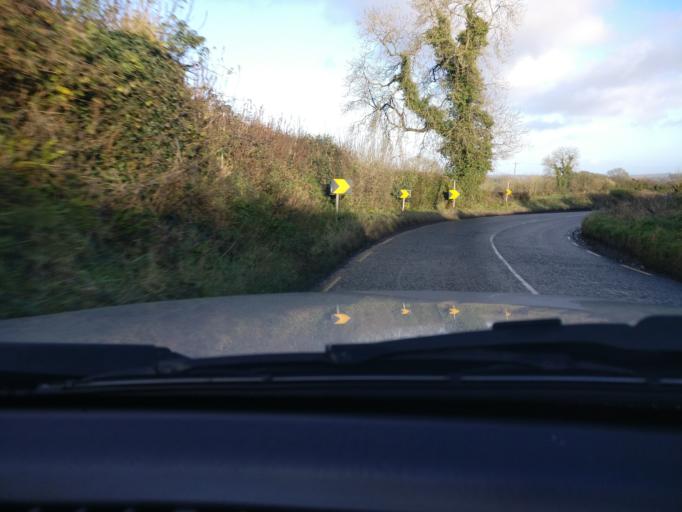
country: IE
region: Ulster
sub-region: An Cabhan
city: Mullagh
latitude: 53.7253
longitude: -6.9910
